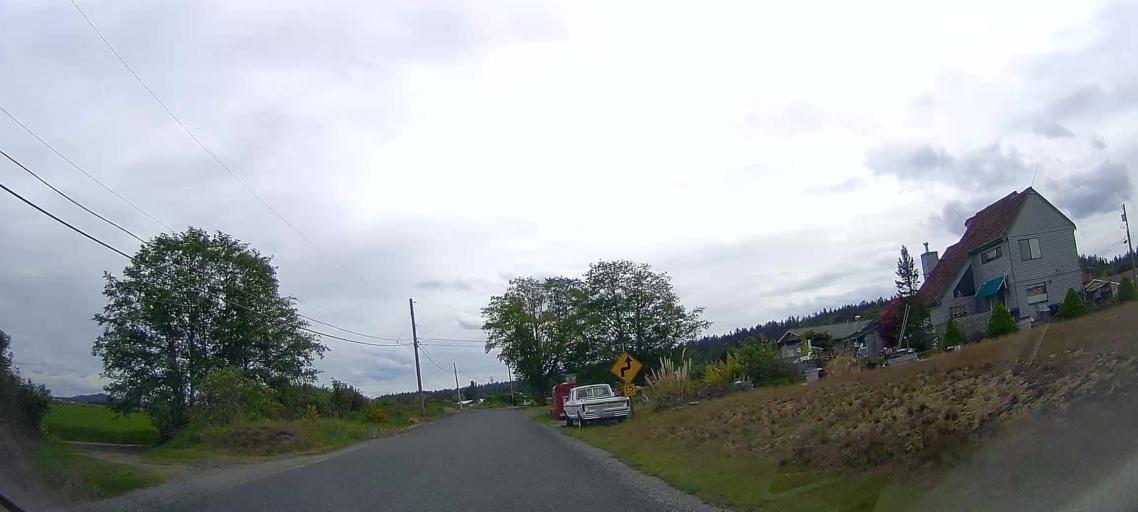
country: US
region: Washington
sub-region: Skagit County
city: Anacortes
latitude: 48.4284
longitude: -122.4970
